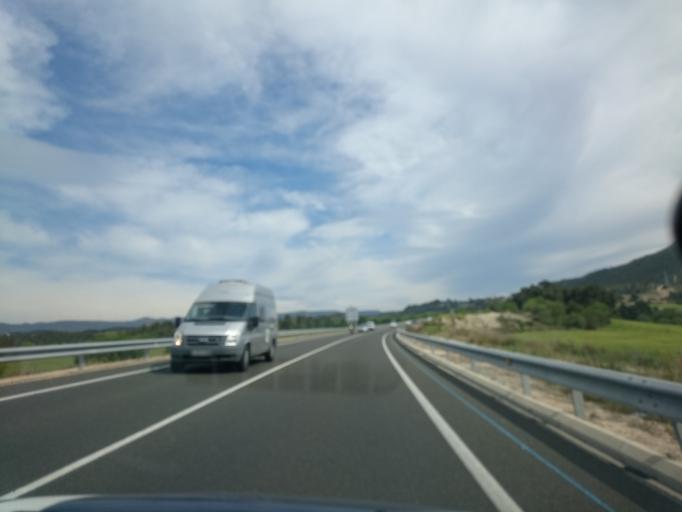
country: ES
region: Catalonia
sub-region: Provincia de Barcelona
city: Odena
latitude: 41.5913
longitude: 1.6621
